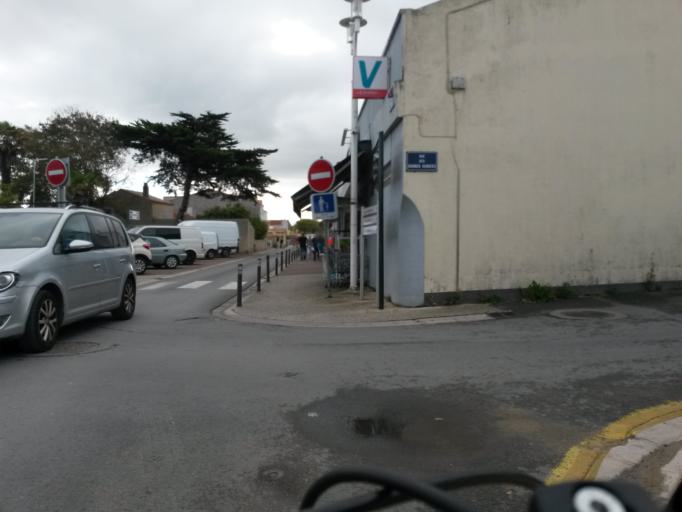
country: FR
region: Poitou-Charentes
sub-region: Departement de la Charente-Maritime
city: Dolus-d'Oleron
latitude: 45.9177
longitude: -1.3318
